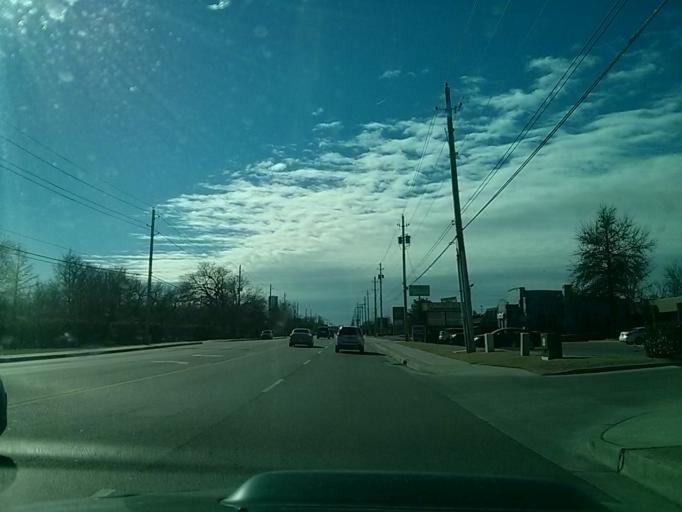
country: US
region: Oklahoma
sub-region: Tulsa County
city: Jenks
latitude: 36.0720
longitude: -95.9580
